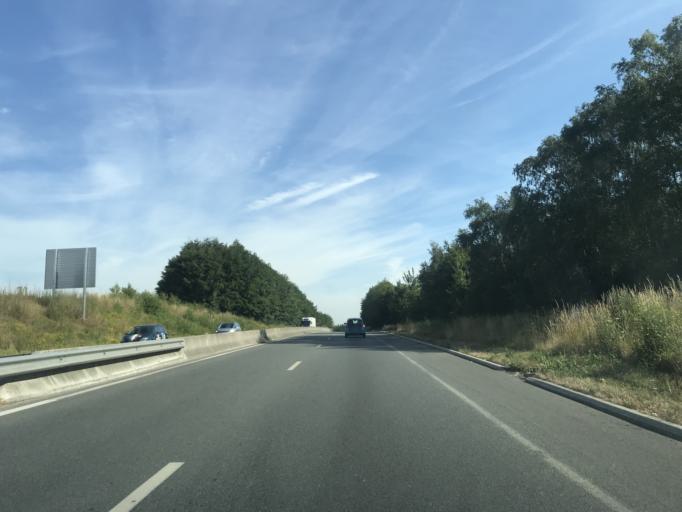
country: FR
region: Haute-Normandie
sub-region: Departement de la Seine-Maritime
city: Barentin
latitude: 49.5279
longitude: 0.9623
